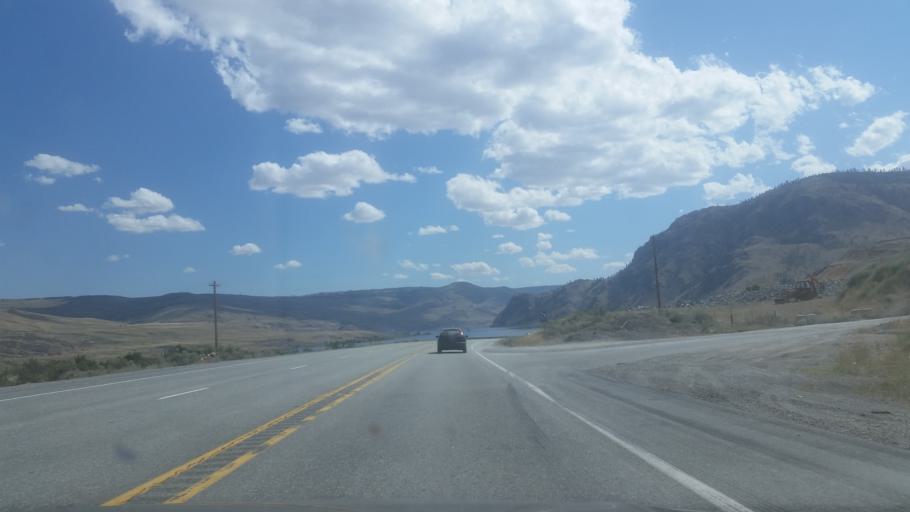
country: US
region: Washington
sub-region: Okanogan County
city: Brewster
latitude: 47.9996
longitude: -119.8841
